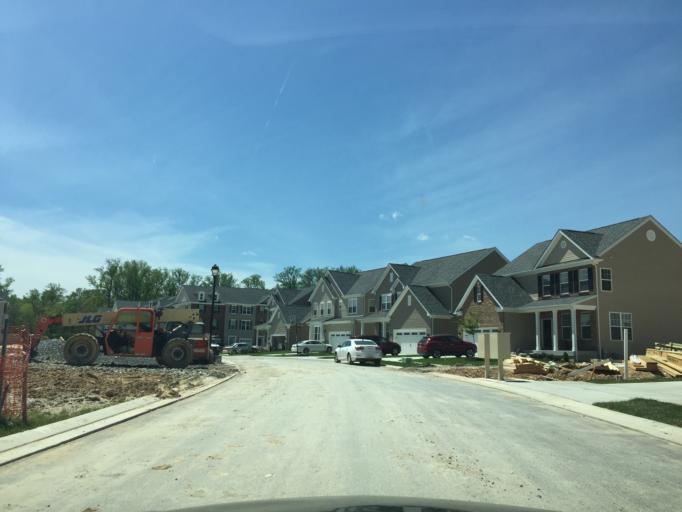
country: US
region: Maryland
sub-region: Baltimore County
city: White Marsh
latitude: 39.3572
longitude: -76.4148
